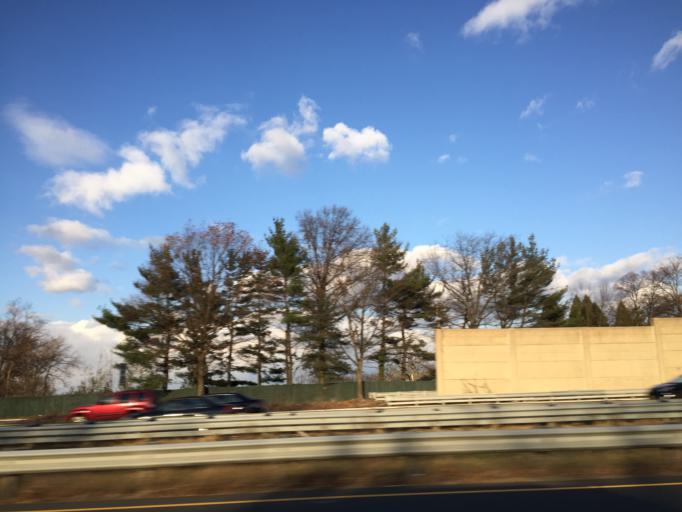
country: US
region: New Jersey
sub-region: Union County
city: Summit
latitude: 40.7355
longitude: -74.3582
